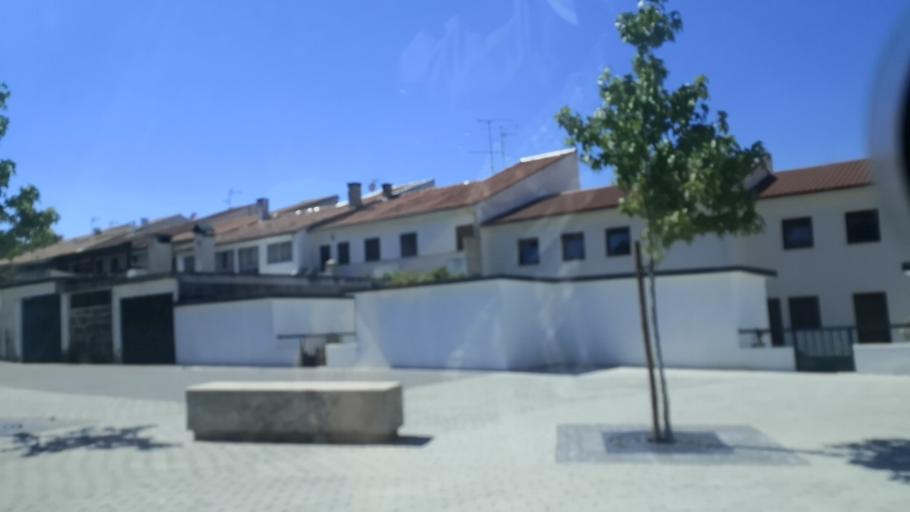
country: PT
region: Braganca
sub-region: Braganca Municipality
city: Braganca
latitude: 41.8100
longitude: -6.7556
